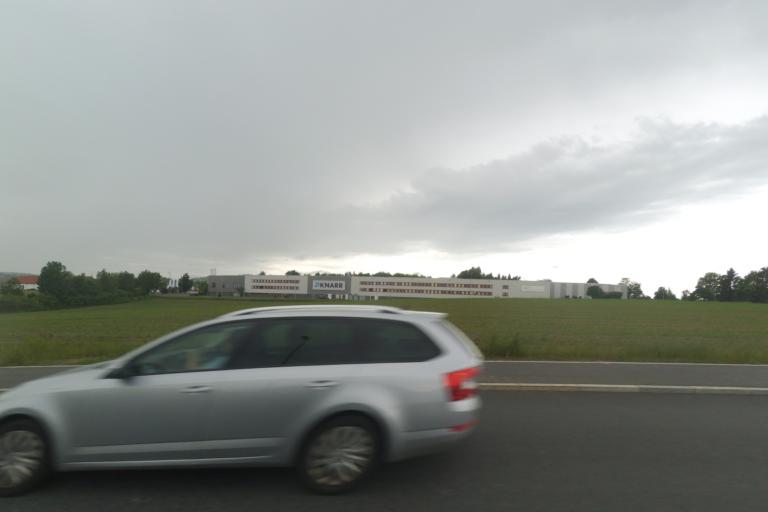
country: DE
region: Bavaria
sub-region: Upper Franconia
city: Helmbrechts
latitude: 50.2313
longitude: 11.7321
